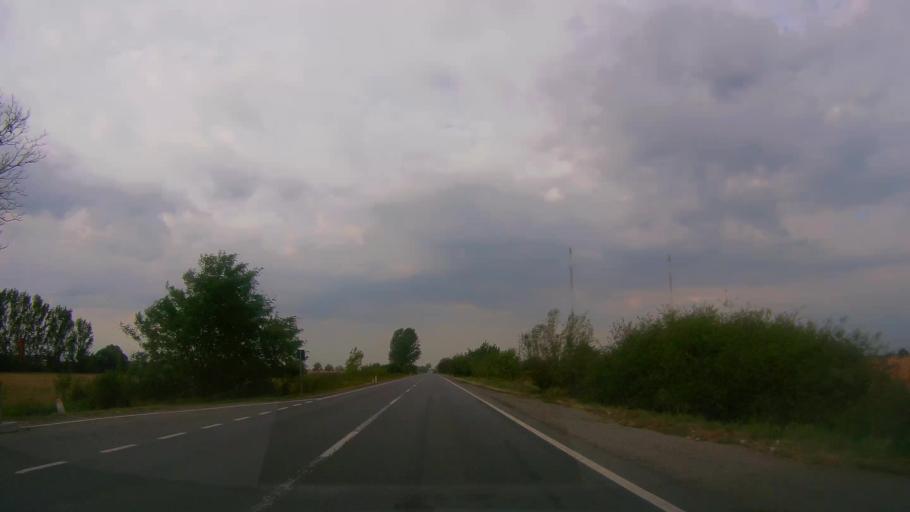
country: RO
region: Satu Mare
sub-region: Comuna Agris
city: Agris
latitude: 47.8572
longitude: 22.9816
